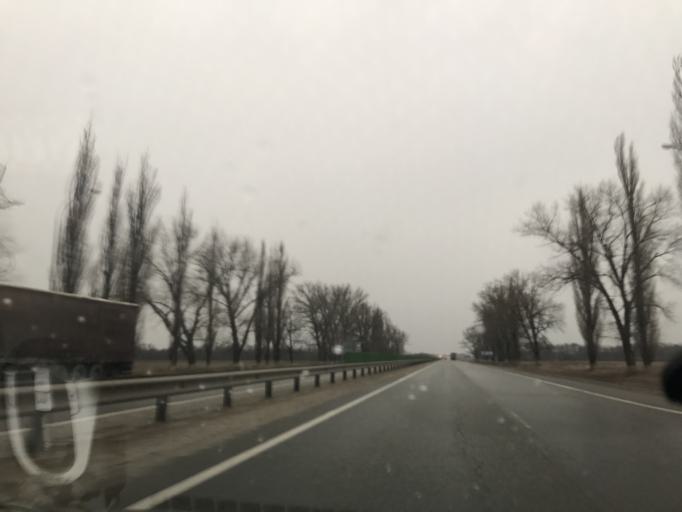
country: RU
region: Krasnodarskiy
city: Pavlovskaya
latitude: 46.2284
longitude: 39.8315
